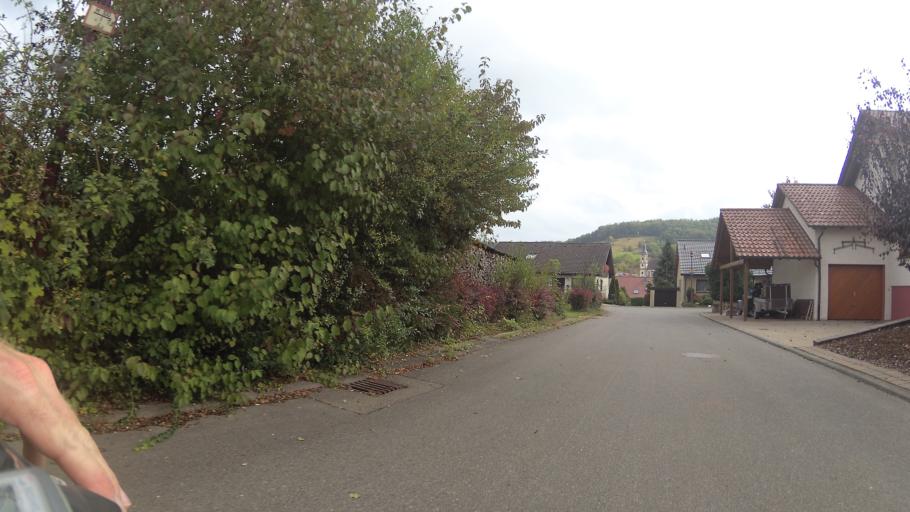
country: DE
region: Baden-Wuerttemberg
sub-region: Regierungsbezirk Stuttgart
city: Eberstadt
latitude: 49.2114
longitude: 9.2982
